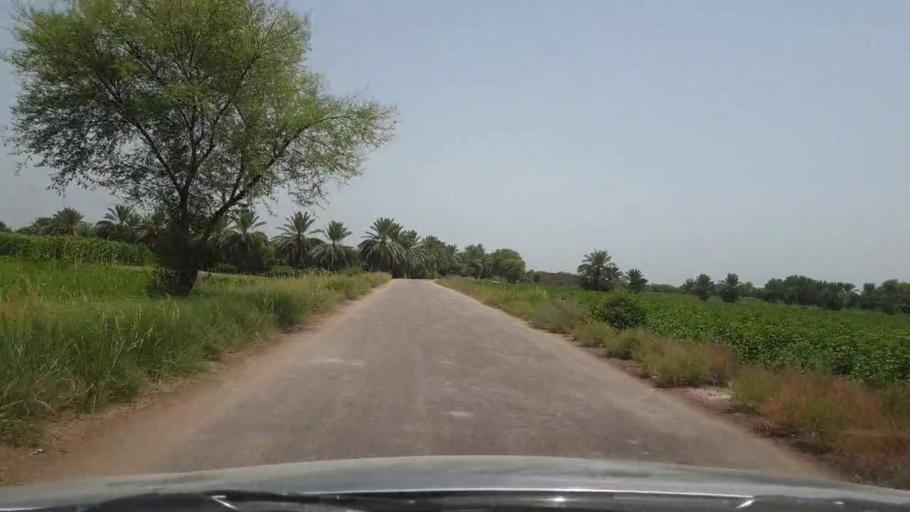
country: PK
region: Sindh
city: Pano Aqil
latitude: 27.8780
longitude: 69.1479
